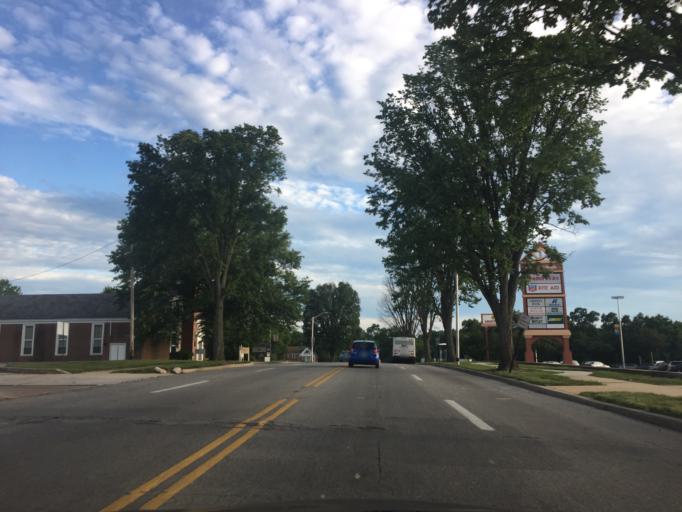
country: US
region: Maryland
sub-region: Baltimore County
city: Towson
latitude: 39.3588
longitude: -76.5947
